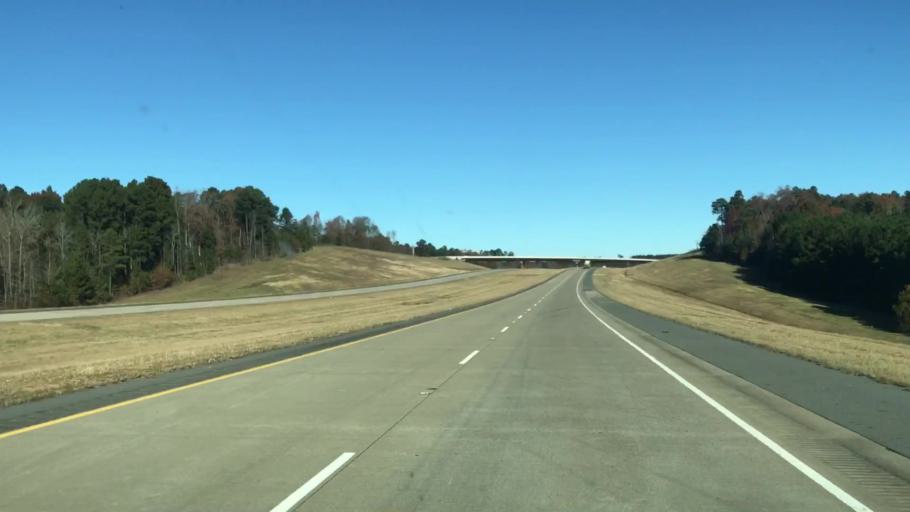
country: US
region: Louisiana
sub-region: Caddo Parish
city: Vivian
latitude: 32.9732
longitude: -93.9080
